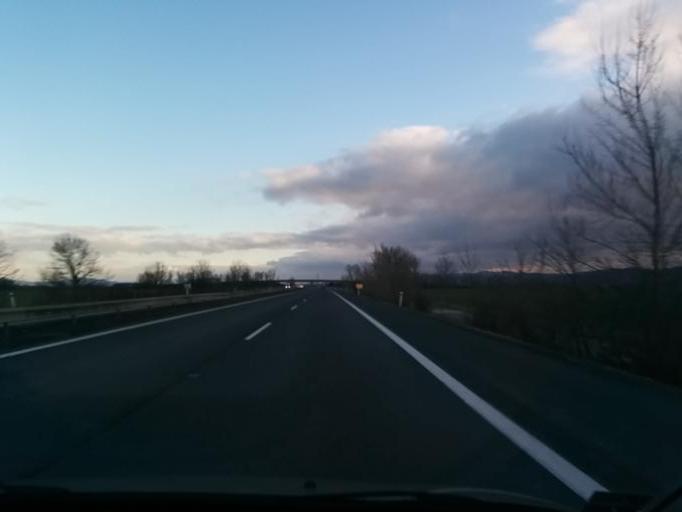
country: SK
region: Trnavsky
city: Leopoldov
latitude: 48.5159
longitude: 17.7741
